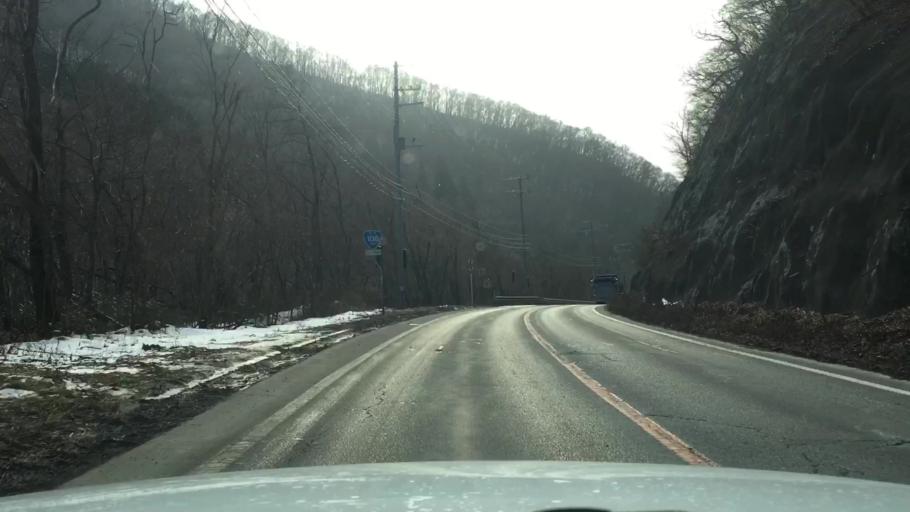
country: JP
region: Iwate
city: Tono
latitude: 39.6300
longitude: 141.5217
